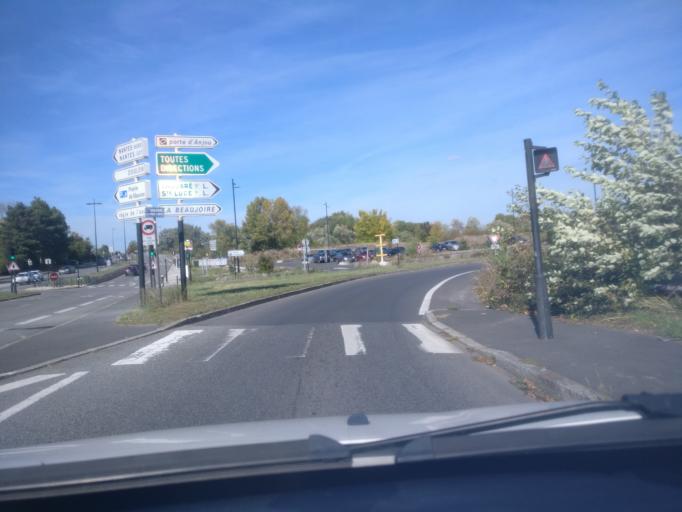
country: FR
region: Pays de la Loire
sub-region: Departement de la Loire-Atlantique
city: Saint-Sebastien-sur-Loire
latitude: 47.2194
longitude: -1.5160
